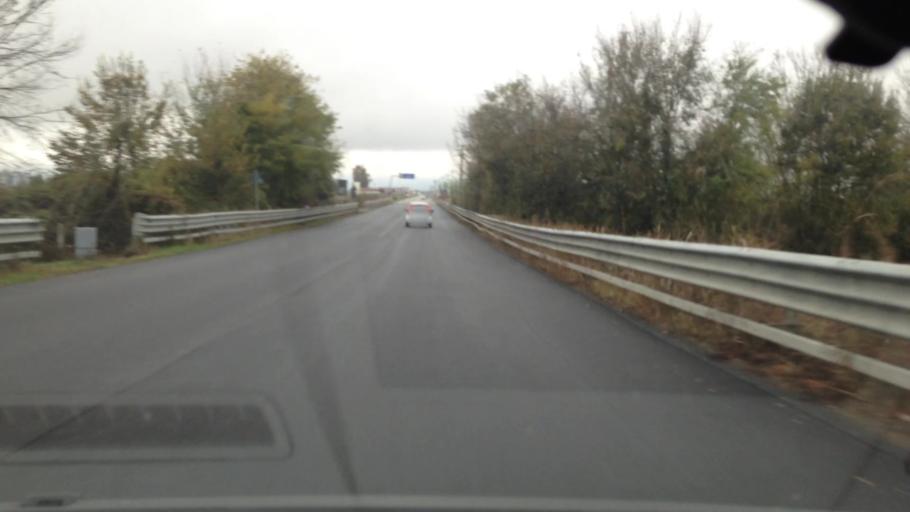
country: IT
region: Piedmont
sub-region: Provincia di Torino
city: Riva Presso Chieri
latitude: 44.9654
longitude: 7.9039
